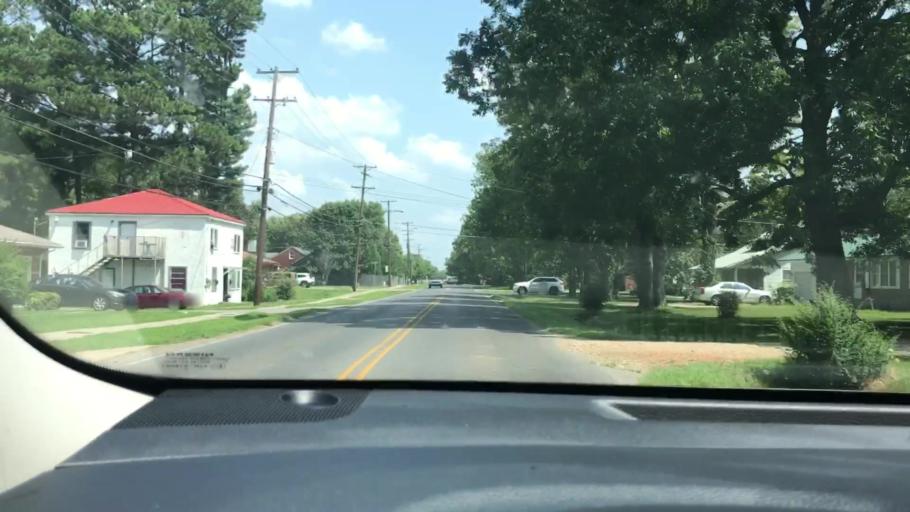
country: US
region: Kentucky
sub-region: Calloway County
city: Murray
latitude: 36.6027
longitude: -88.3080
